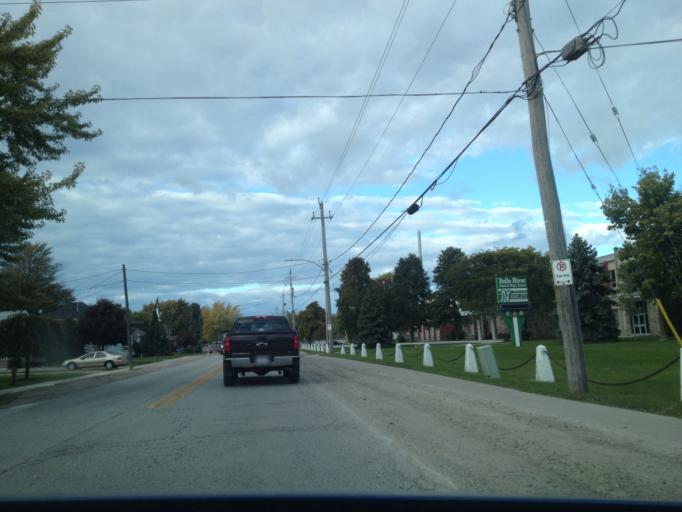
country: US
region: Michigan
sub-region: Wayne County
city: Grosse Pointe Farms
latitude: 42.2878
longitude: -82.7121
